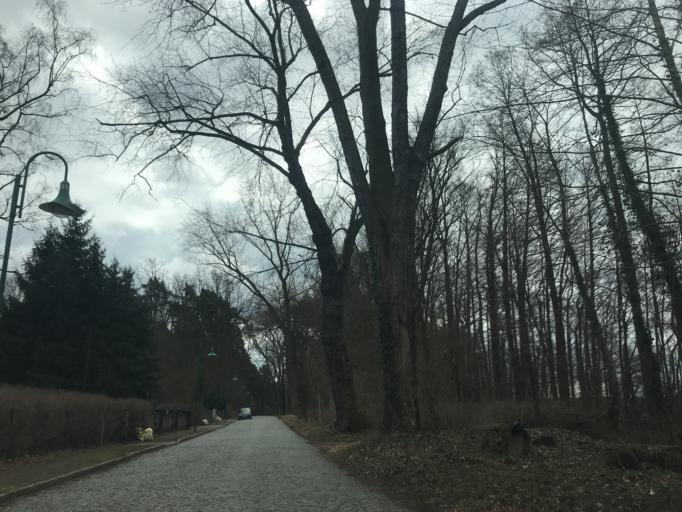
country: DE
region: Brandenburg
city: Zossen
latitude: 52.1536
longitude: 13.4737
